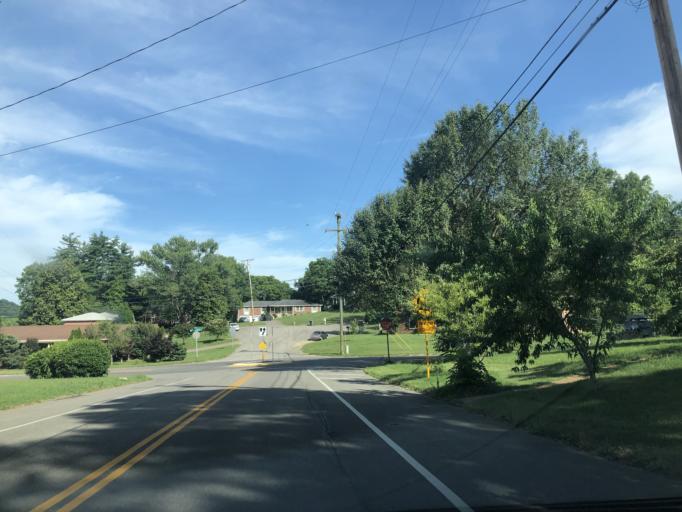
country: US
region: Tennessee
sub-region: Davidson County
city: Belle Meade
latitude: 36.0601
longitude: -86.9352
